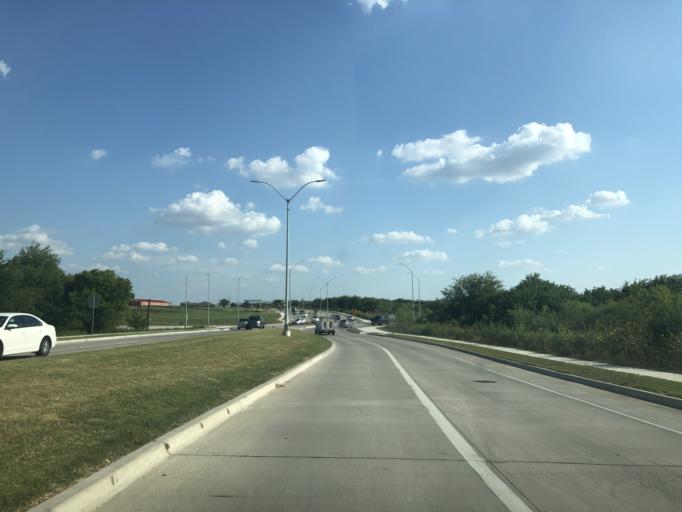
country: US
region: Texas
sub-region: Tarrant County
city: Saginaw
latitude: 32.8493
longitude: -97.3907
